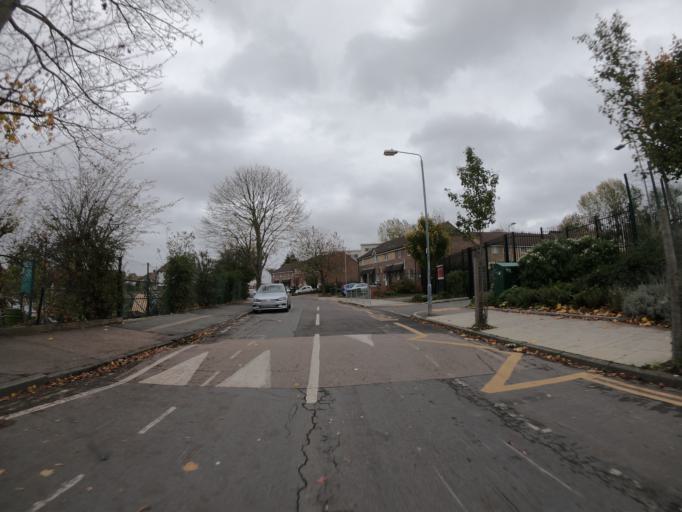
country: GB
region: England
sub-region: Greater London
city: Blackheath
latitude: 51.4814
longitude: 0.0273
